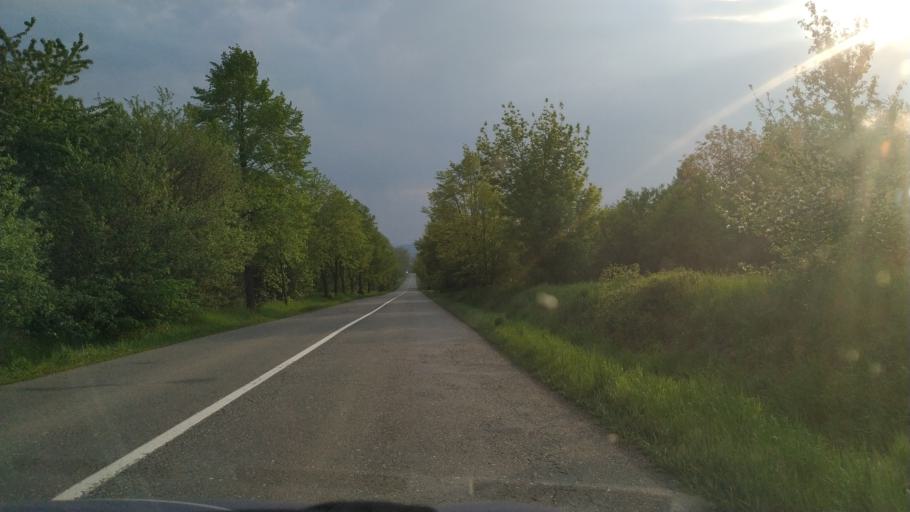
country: CZ
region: Olomoucky
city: Hnevotin
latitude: 49.5671
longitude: 17.1694
